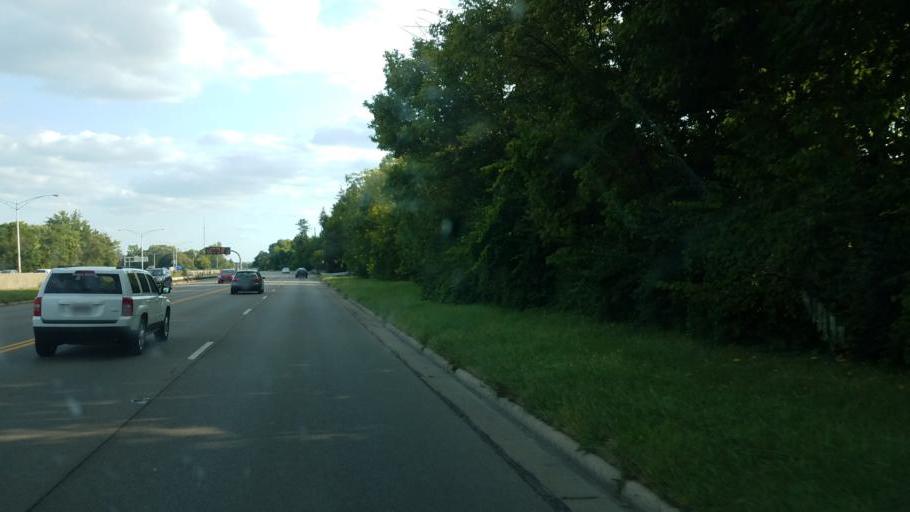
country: US
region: Ohio
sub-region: Franklin County
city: Worthington
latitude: 40.0462
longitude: -83.0339
